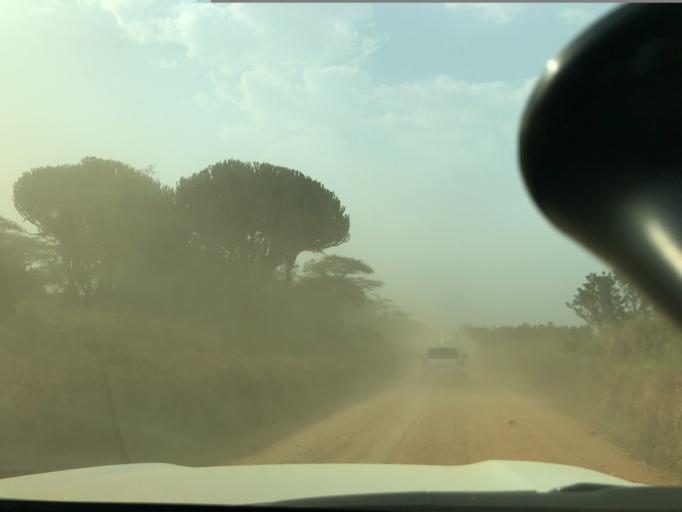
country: UG
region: Western Region
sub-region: Kasese District
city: Kilembe
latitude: 0.0647
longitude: 29.6615
